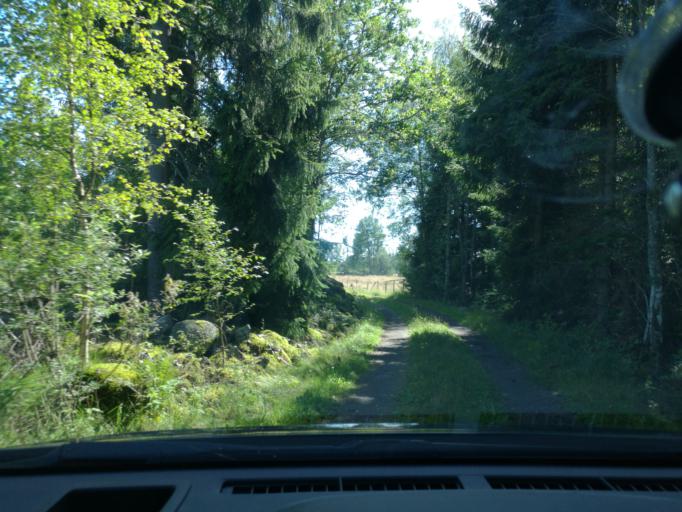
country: SE
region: Kronoberg
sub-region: Alvesta Kommun
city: Vislanda
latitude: 56.6932
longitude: 14.3983
